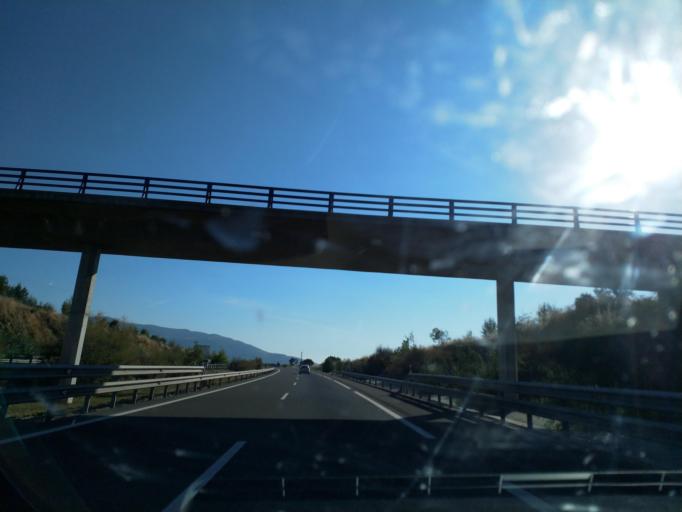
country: ES
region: Castille and Leon
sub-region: Provincia de Segovia
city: Segovia
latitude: 40.8933
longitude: -4.1128
